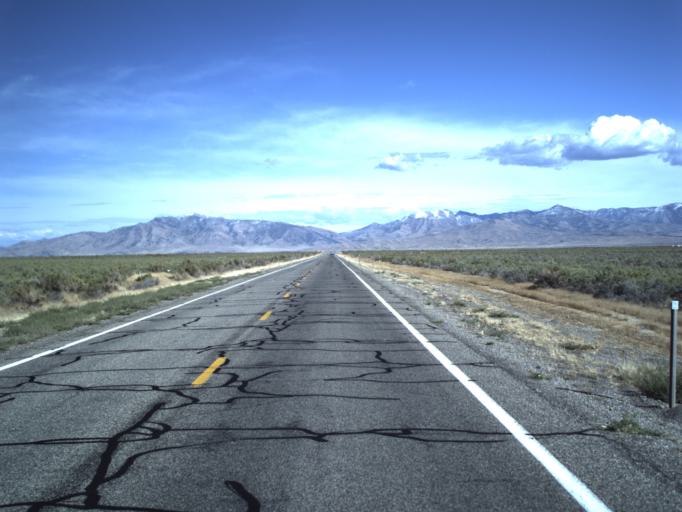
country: US
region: Utah
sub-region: Millard County
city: Delta
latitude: 39.3531
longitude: -112.5153
